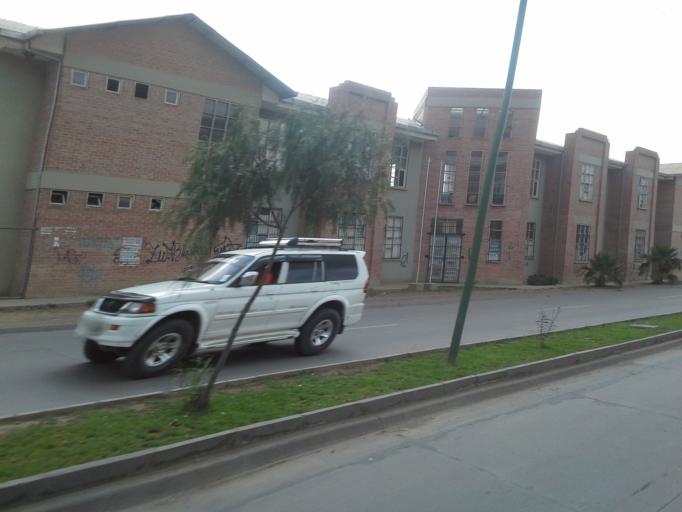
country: BO
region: Cochabamba
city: Cochabamba
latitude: -17.4325
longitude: -66.1495
